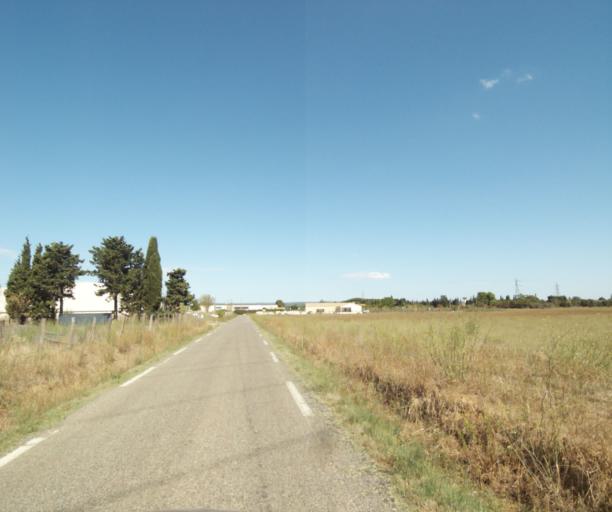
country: FR
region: Languedoc-Roussillon
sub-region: Departement du Gard
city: Rodilhan
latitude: 43.8165
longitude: 4.4292
